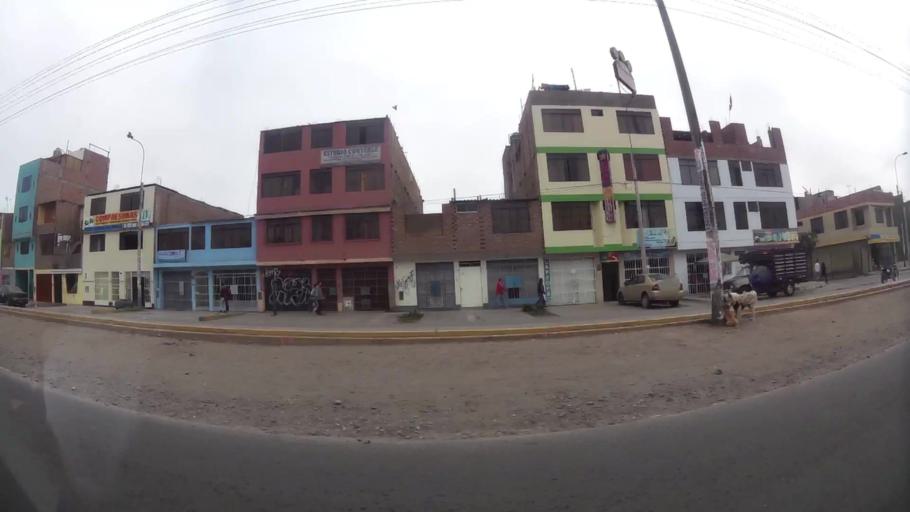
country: PE
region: Lima
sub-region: Lima
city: Independencia
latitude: -12.0159
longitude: -77.0782
